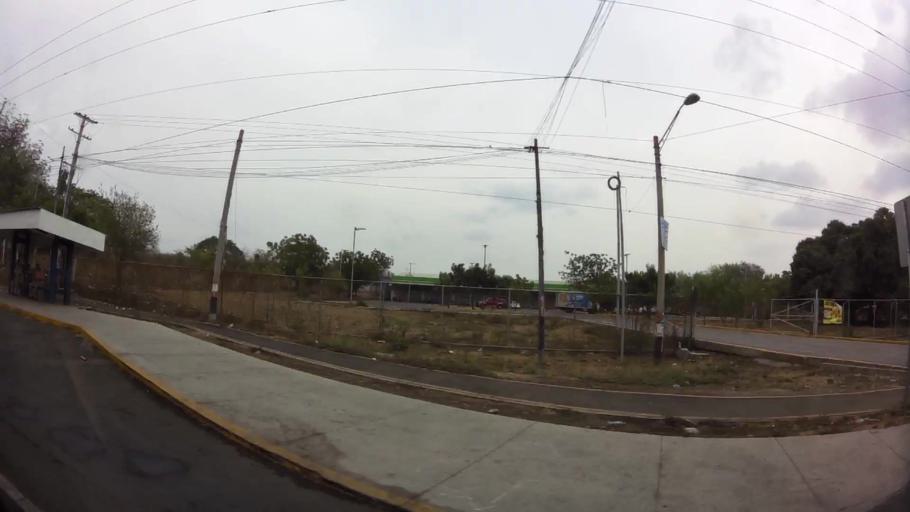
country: NI
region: Leon
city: Leon
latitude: 12.4570
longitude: -86.8669
